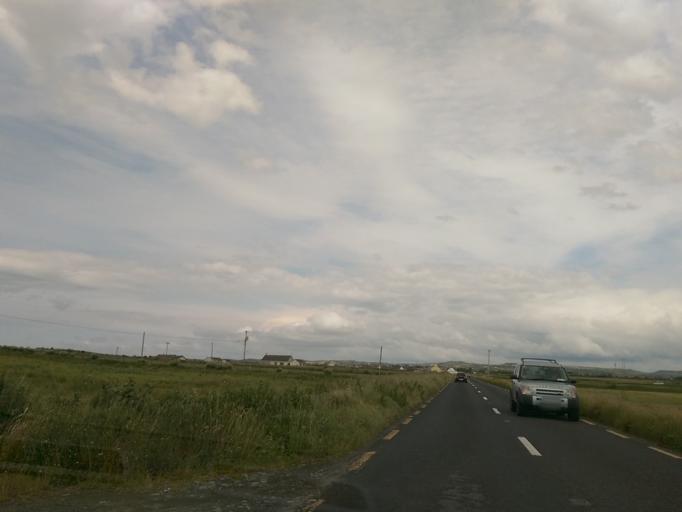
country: IE
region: Munster
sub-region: An Clar
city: Kilrush
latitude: 52.8299
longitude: -9.4354
